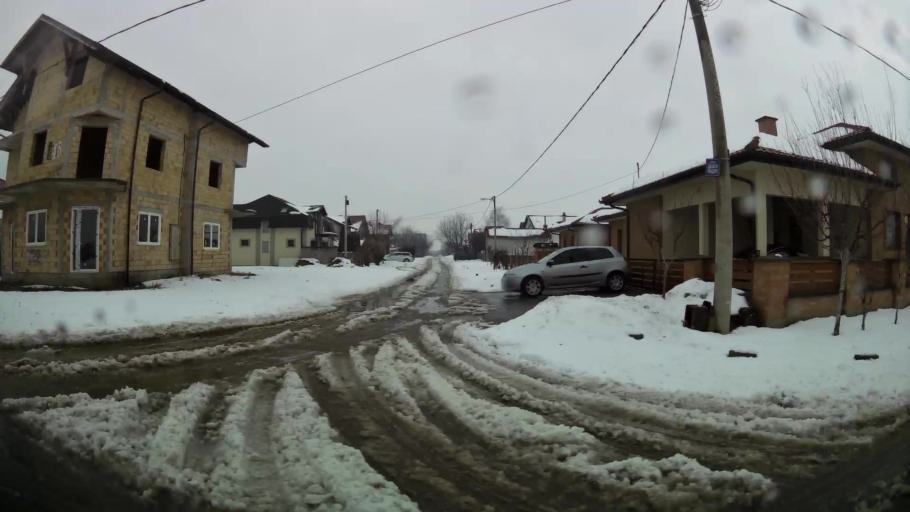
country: RS
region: Central Serbia
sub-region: Belgrade
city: Zemun
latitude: 44.8590
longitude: 20.3438
